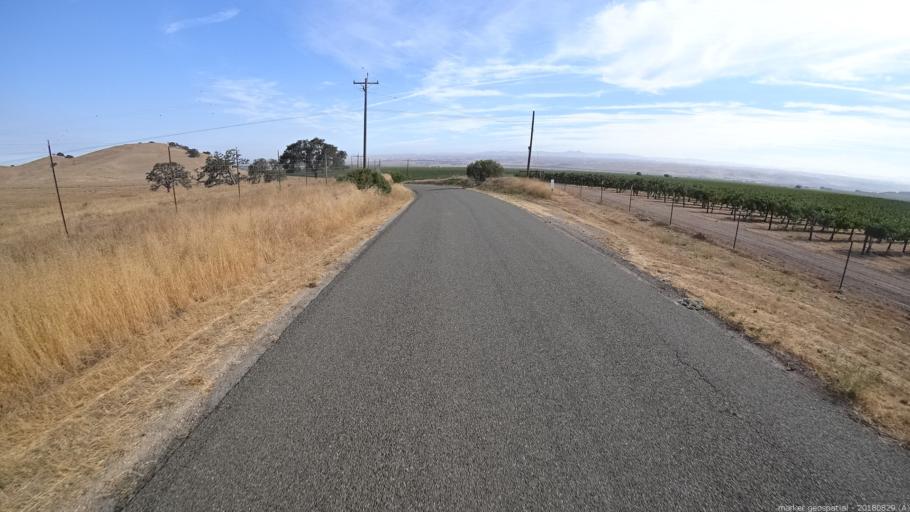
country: US
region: California
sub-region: Monterey County
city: King City
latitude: 36.0743
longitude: -121.0381
